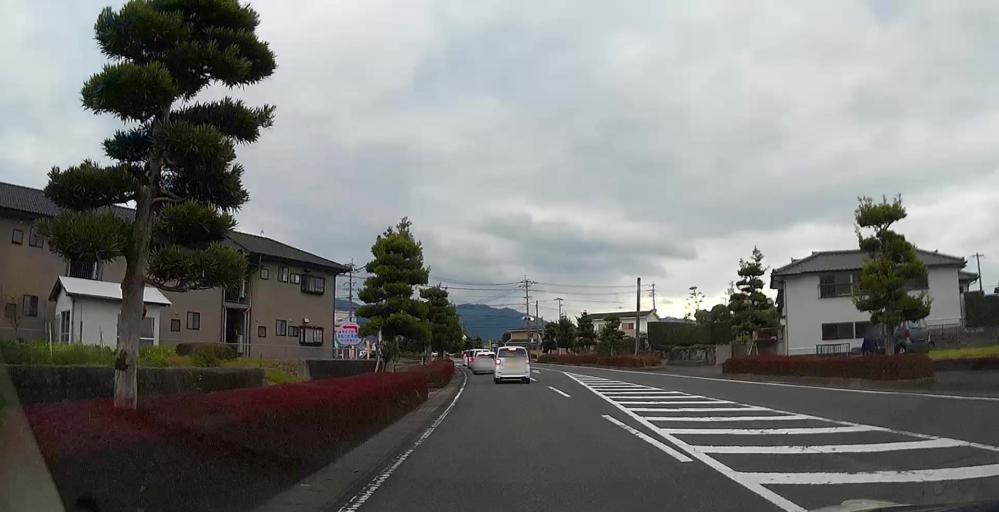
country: JP
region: Kagoshima
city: Izumi
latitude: 32.0817
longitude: 130.3444
